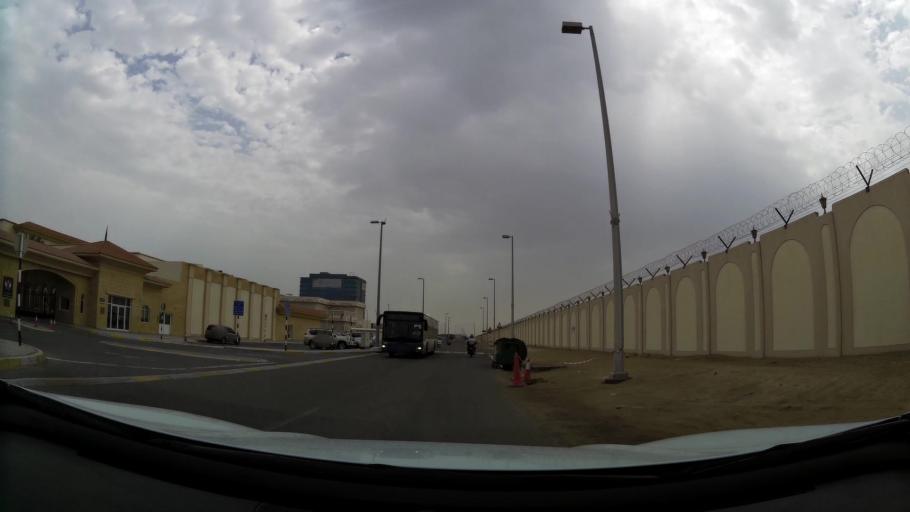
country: AE
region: Abu Dhabi
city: Abu Dhabi
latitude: 24.4291
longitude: 54.4599
